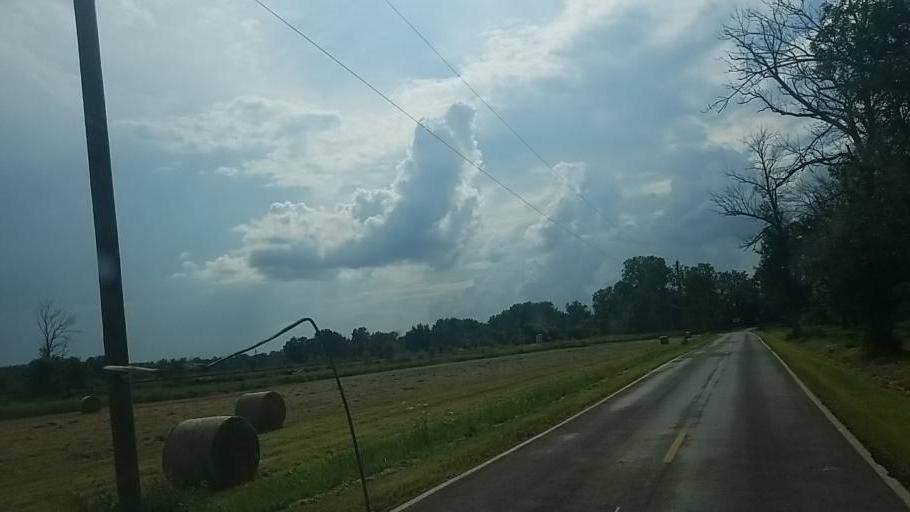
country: US
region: Ohio
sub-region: Medina County
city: Westfield Center
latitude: 40.9950
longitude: -81.9390
